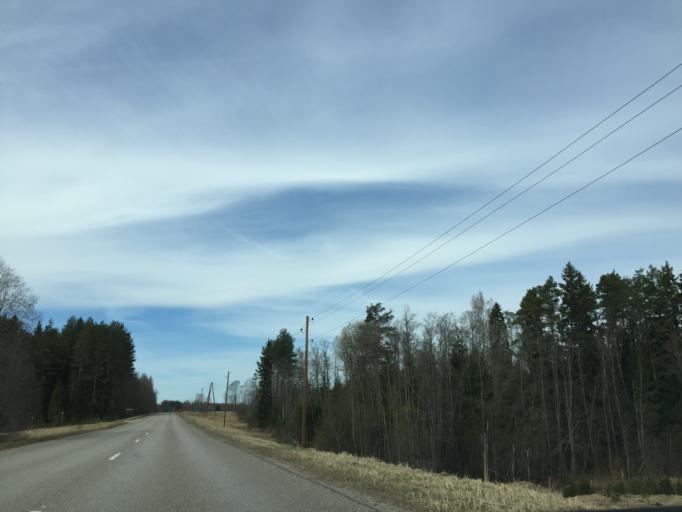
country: LV
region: Valkas Rajons
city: Valka
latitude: 57.7941
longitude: 25.8740
